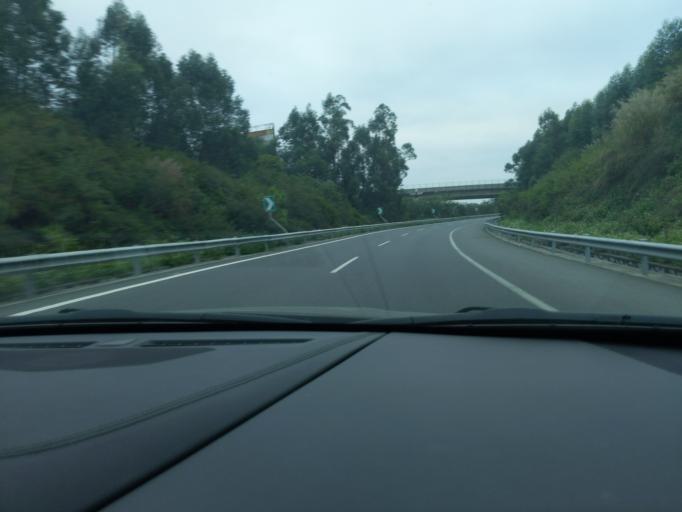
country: CN
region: Fujian
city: Neikeng
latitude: 24.7863
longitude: 118.4765
